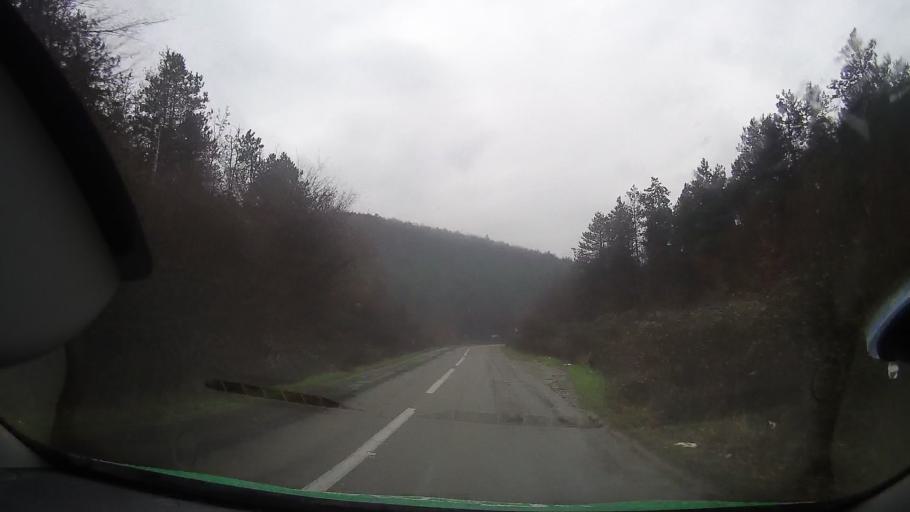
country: RO
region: Bihor
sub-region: Comuna Holod
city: Vintere
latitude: 46.7705
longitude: 22.1706
